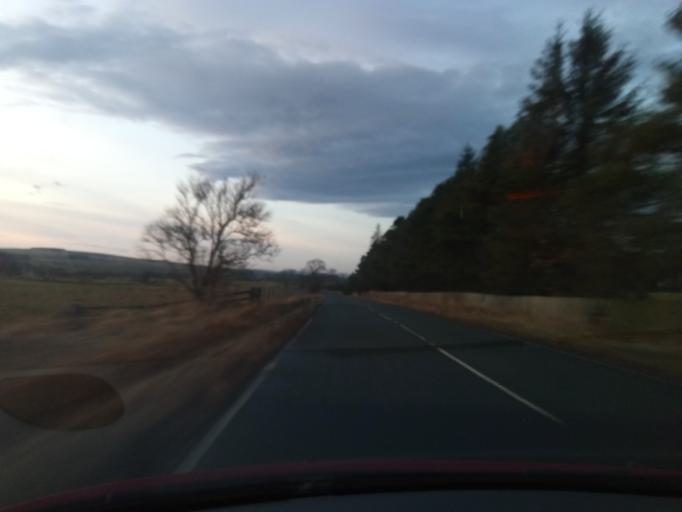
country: GB
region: England
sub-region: Northumberland
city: Otterburn
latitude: 55.2377
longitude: -2.1995
